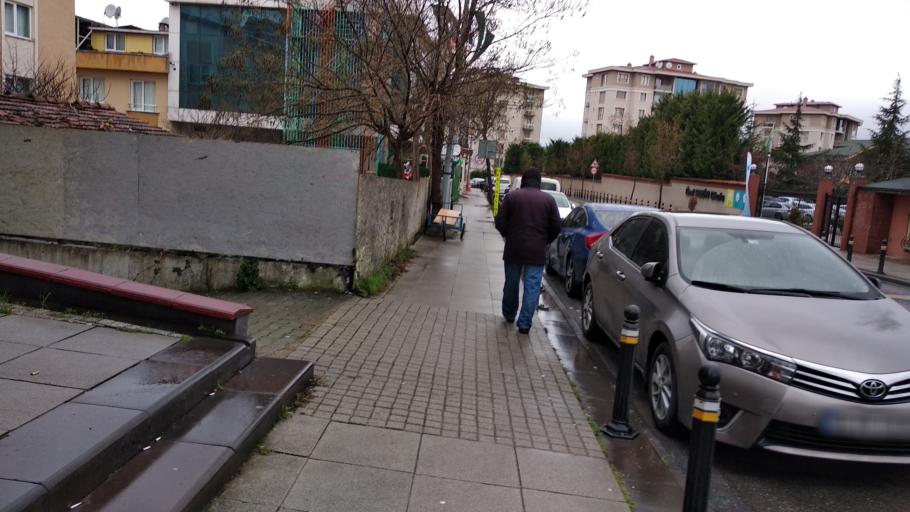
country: TR
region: Istanbul
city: Samandira
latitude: 41.0235
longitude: 29.1843
